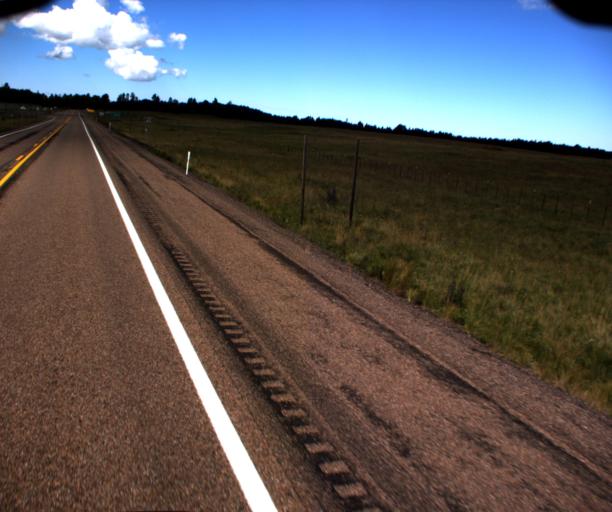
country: US
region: Arizona
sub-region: Apache County
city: Eagar
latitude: 34.0448
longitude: -109.5894
